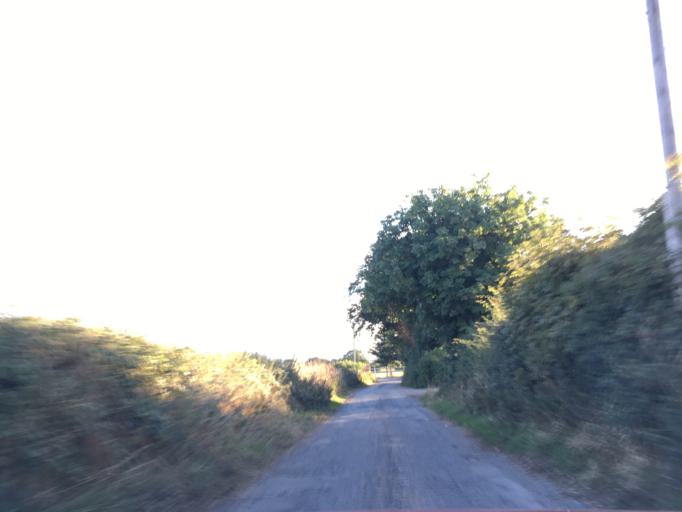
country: IE
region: Munster
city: Cashel
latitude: 52.4891
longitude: -7.9525
